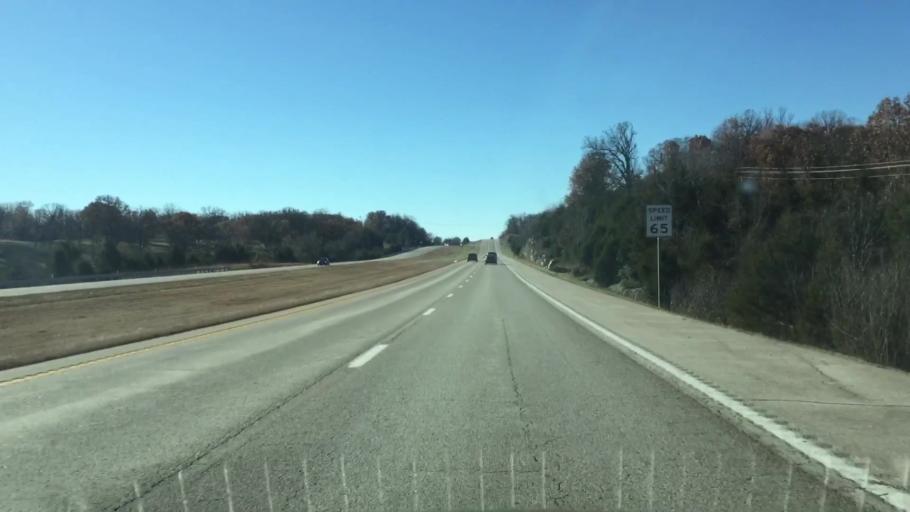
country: US
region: Missouri
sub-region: Cole County
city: Wardsville
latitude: 38.4650
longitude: -92.2937
